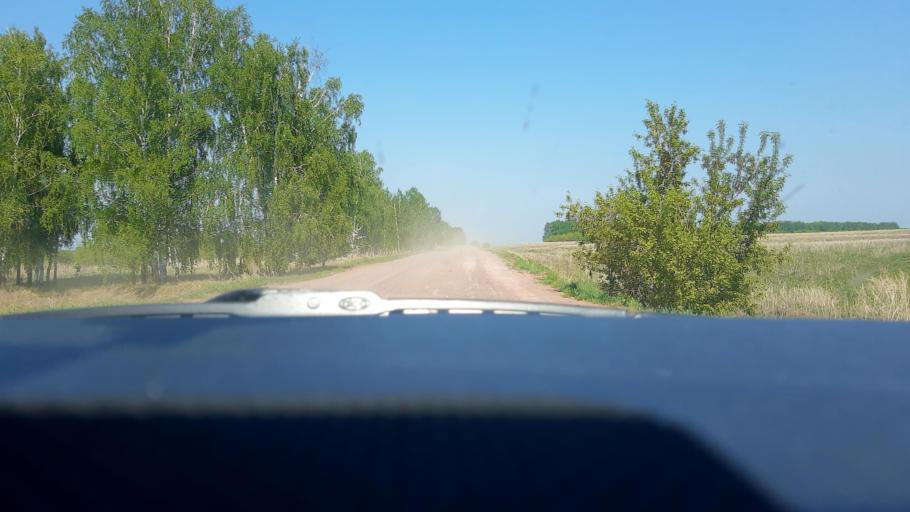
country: RU
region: Bashkortostan
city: Chishmy
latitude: 54.4323
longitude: 55.2957
